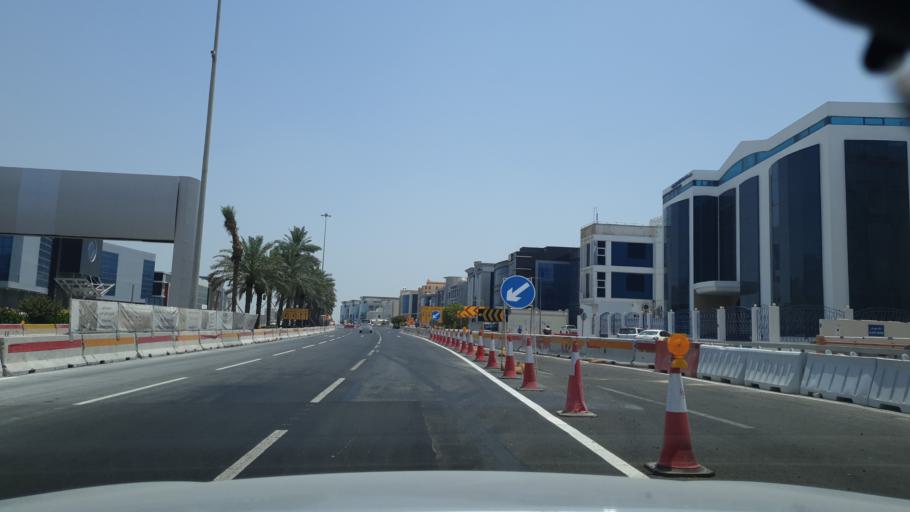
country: QA
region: Baladiyat ad Dawhah
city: Doha
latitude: 25.2567
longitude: 51.5497
